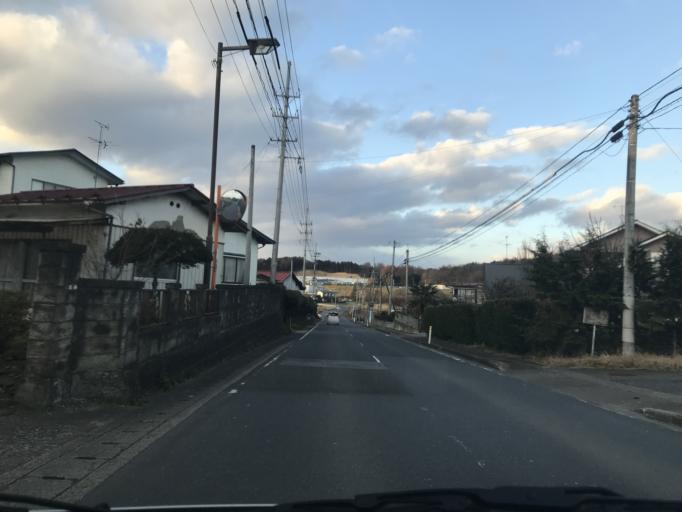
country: JP
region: Miyagi
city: Furukawa
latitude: 38.6629
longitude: 141.0114
